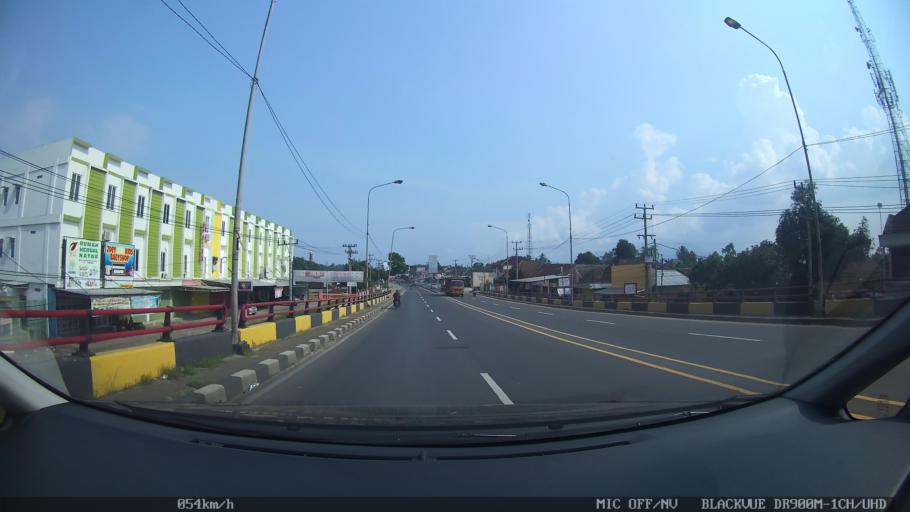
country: ID
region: Lampung
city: Natar
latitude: -5.3218
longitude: 105.2001
